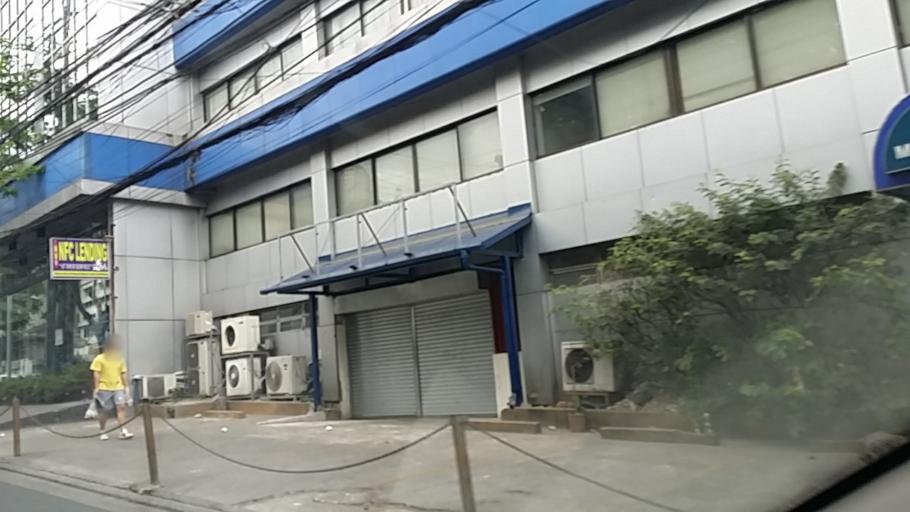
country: PH
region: Metro Manila
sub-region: Mandaluyong
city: Mandaluyong City
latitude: 14.5792
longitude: 121.0492
